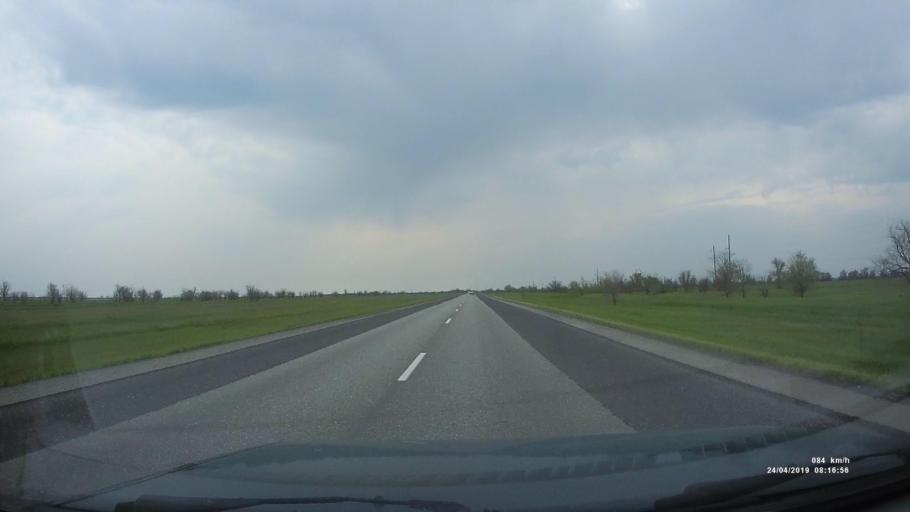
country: RU
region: Kalmykiya
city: Priyutnoye
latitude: 46.0984
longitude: 43.6208
